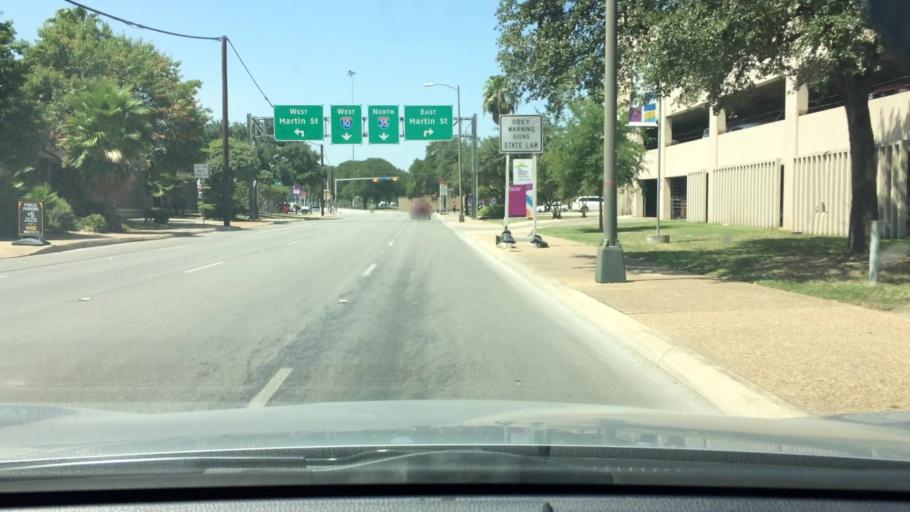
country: US
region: Texas
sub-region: Bexar County
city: San Antonio
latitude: 29.4285
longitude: -98.4998
